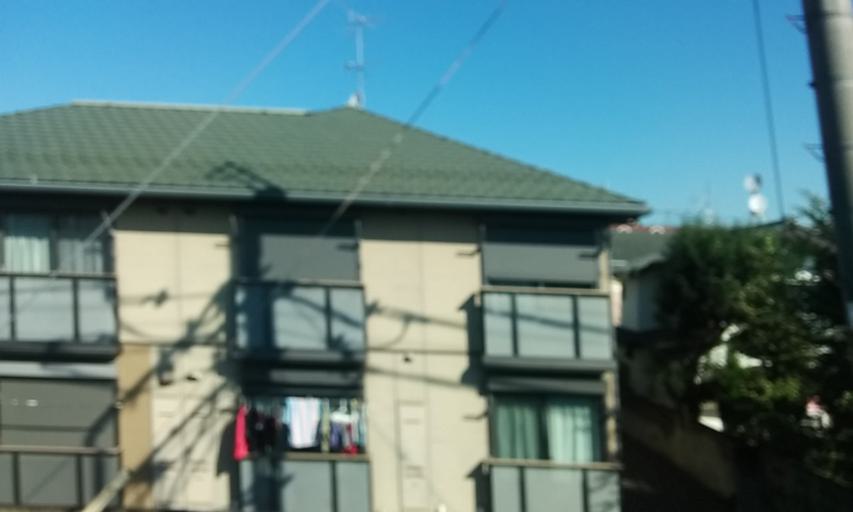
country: JP
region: Tokyo
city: Nishi-Tokyo-shi
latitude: 35.7291
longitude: 139.5596
